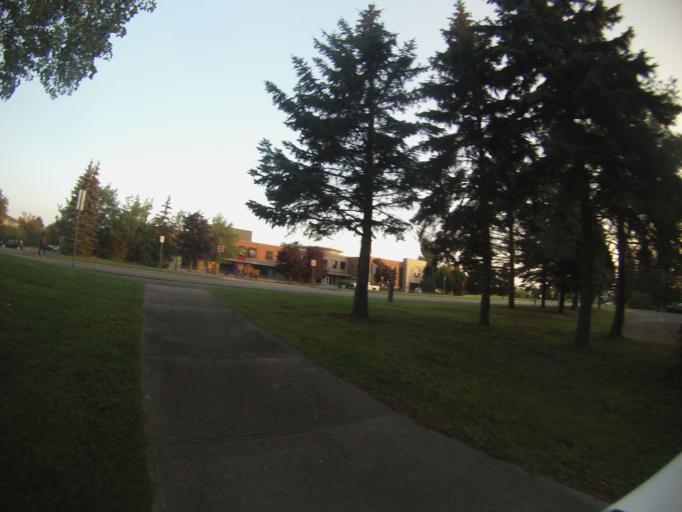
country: CA
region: Ontario
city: Ottawa
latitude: 45.3653
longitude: -75.6270
